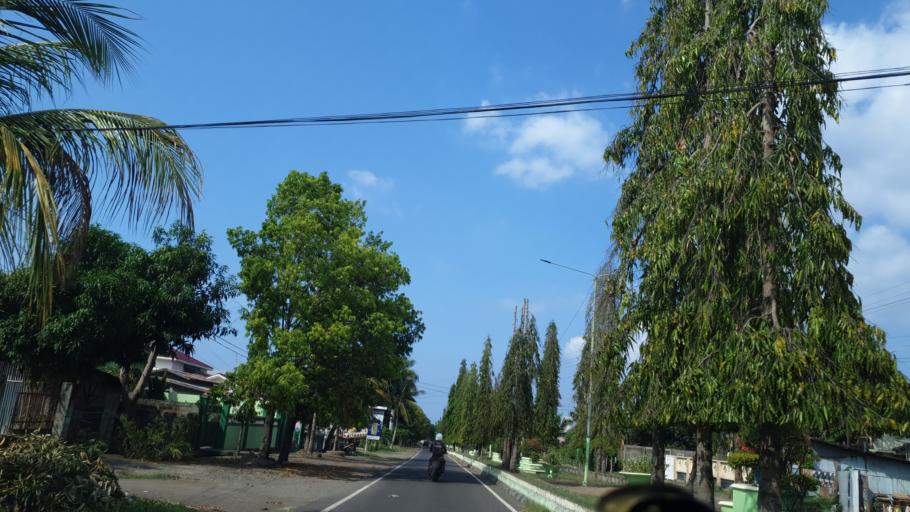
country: ID
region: East Nusa Tenggara
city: Waioti
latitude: -8.6321
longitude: 122.2363
